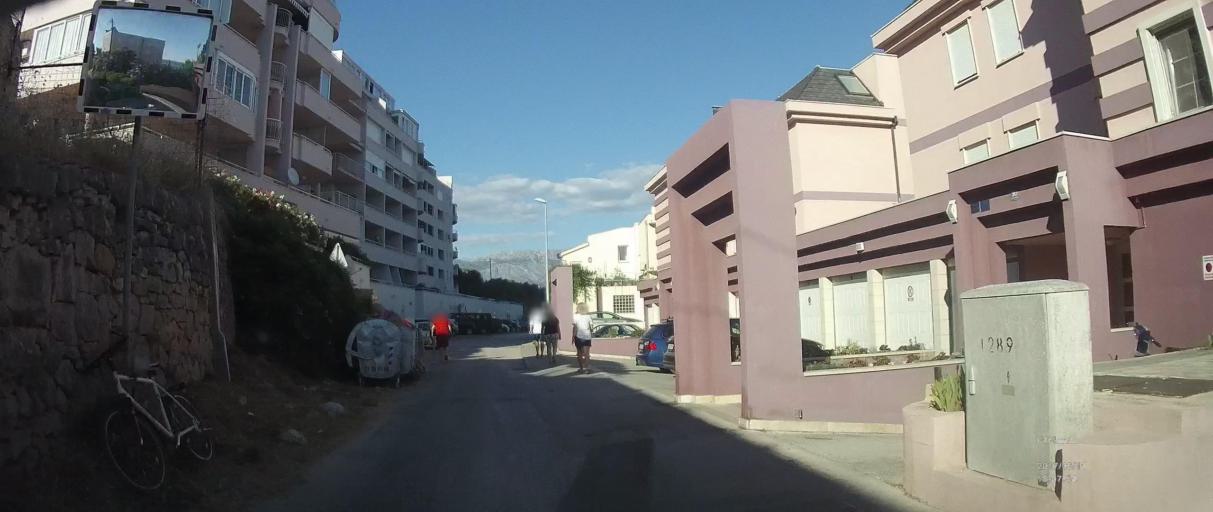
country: HR
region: Splitsko-Dalmatinska
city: Vranjic
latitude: 43.5034
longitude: 16.4732
